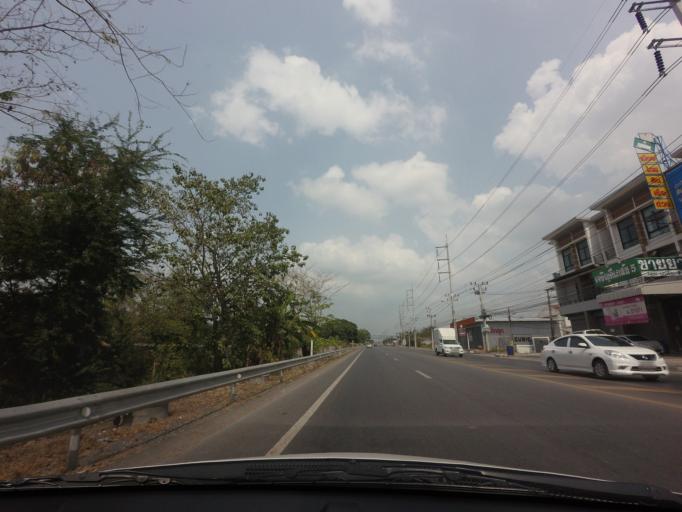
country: TH
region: Pathum Thani
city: Thanyaburi
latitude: 14.0567
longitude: 100.7101
